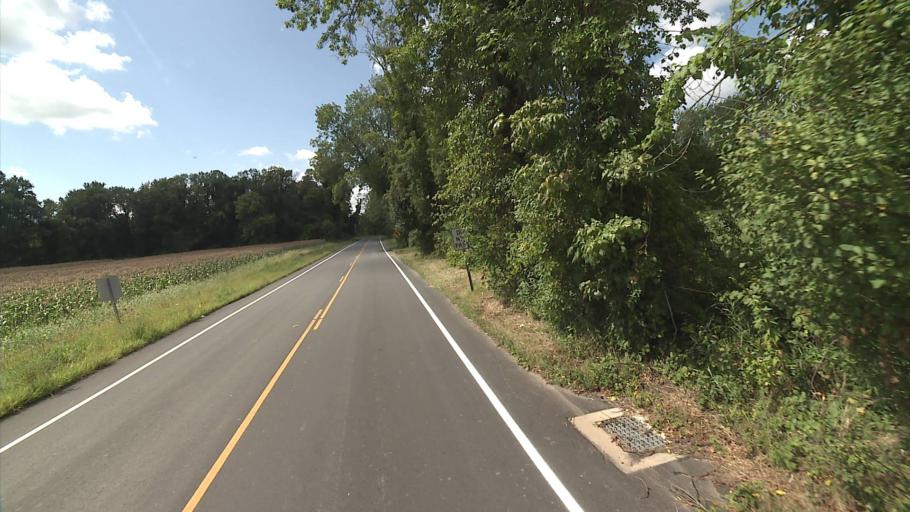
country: US
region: Connecticut
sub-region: Middlesex County
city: Cromwell
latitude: 41.6025
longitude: -72.6128
